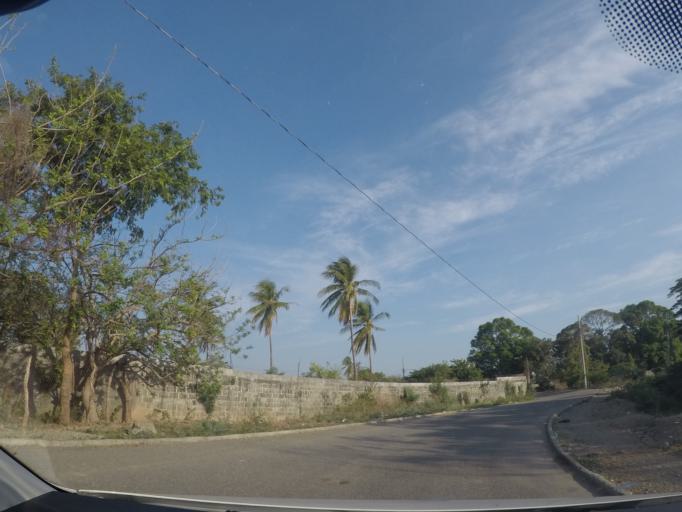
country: MX
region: Oaxaca
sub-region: Santo Domingo Tehuantepec
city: La Noria
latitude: 16.2482
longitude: -95.1490
